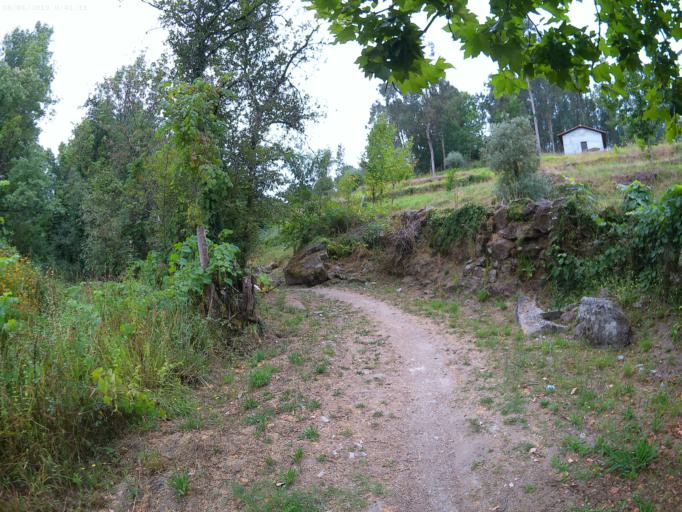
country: PT
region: Viana do Castelo
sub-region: Ponte da Barca
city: Ponte da Barca
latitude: 41.8013
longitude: -8.4739
